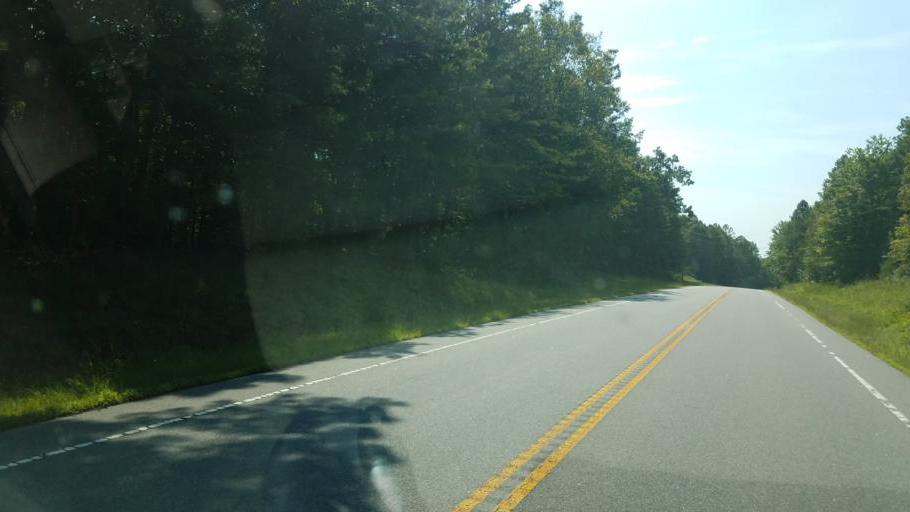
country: US
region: North Carolina
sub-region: Burke County
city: Glen Alpine
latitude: 35.8880
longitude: -81.8023
